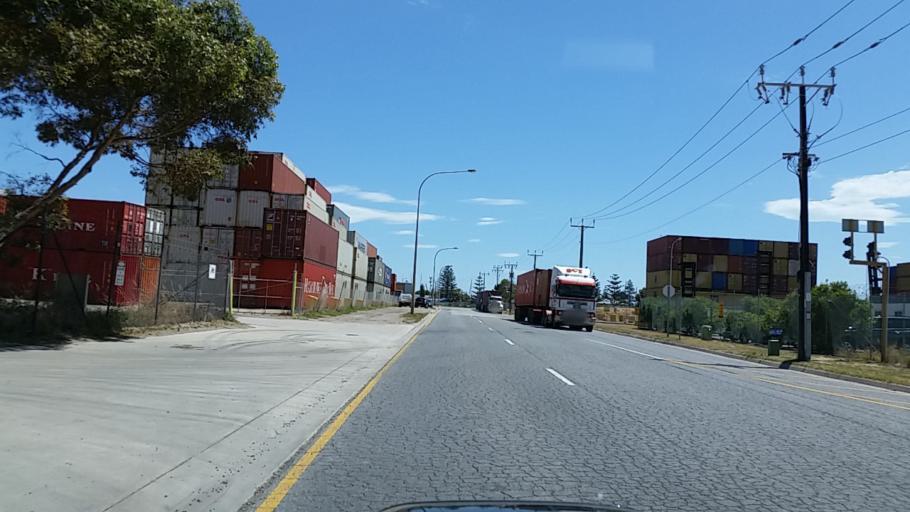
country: AU
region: South Australia
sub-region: Port Adelaide Enfield
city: Birkenhead
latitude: -34.7734
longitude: 138.4938
